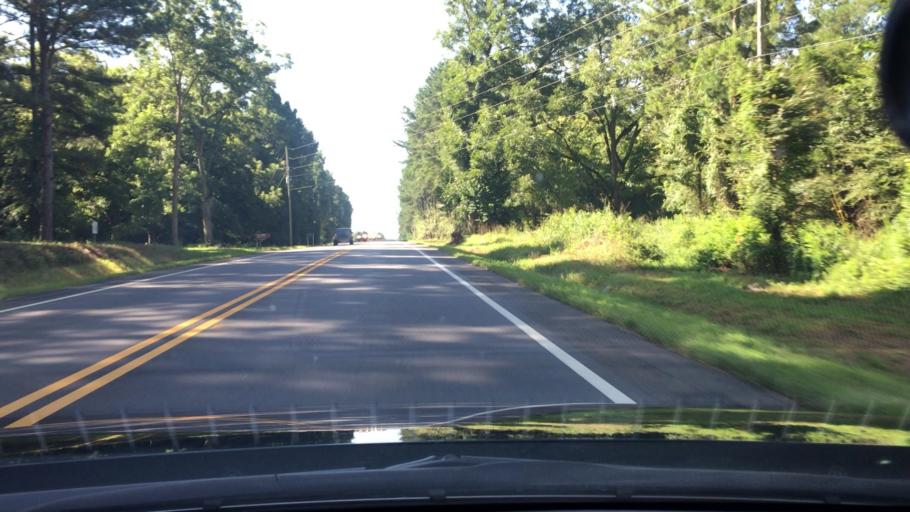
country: US
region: Georgia
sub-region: Putnam County
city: Jefferson
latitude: 33.4622
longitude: -83.4133
